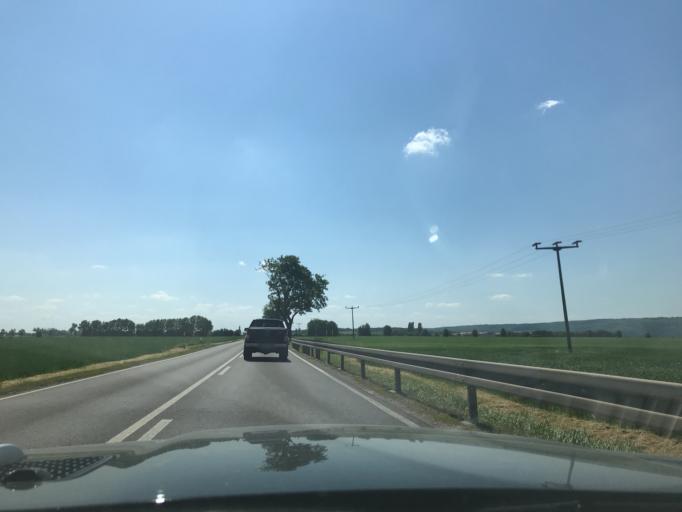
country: DE
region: Thuringia
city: Westhausen
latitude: 51.0083
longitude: 10.6854
